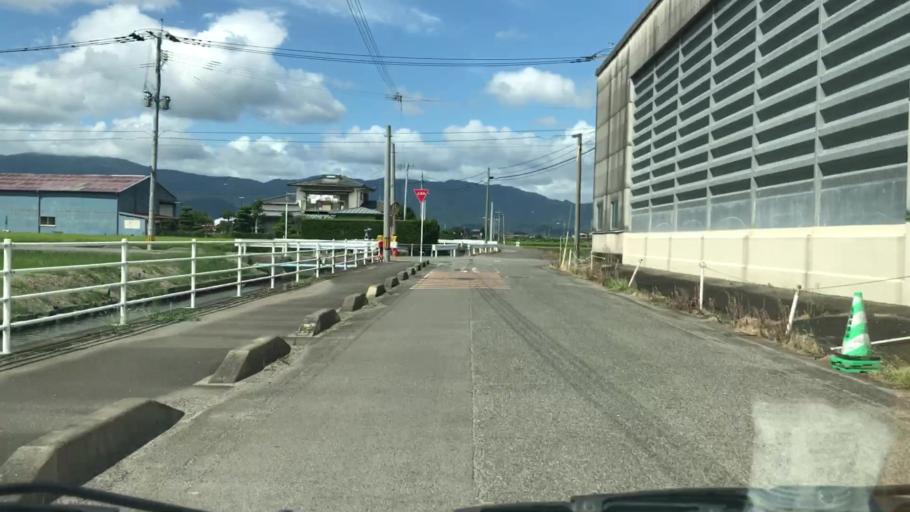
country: JP
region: Saga Prefecture
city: Saga-shi
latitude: 33.2322
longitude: 130.2121
